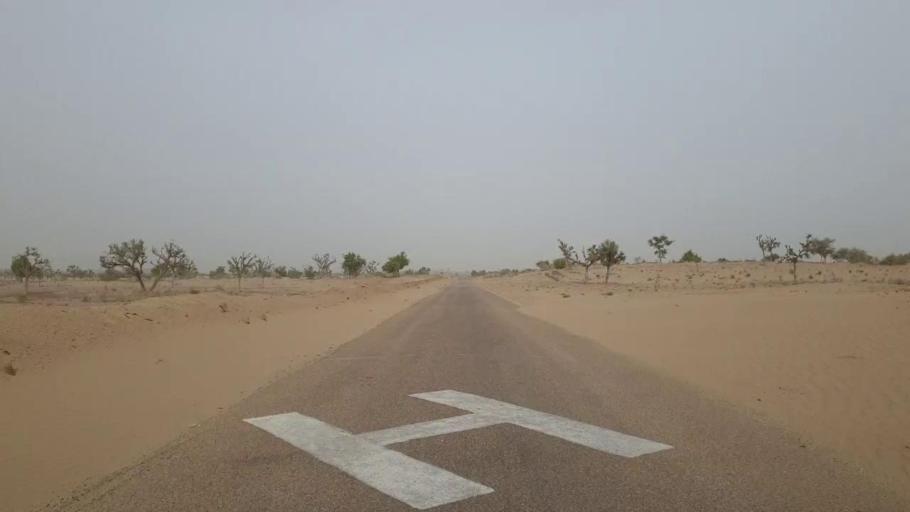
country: PK
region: Sindh
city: Islamkot
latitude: 24.5478
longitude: 70.3653
